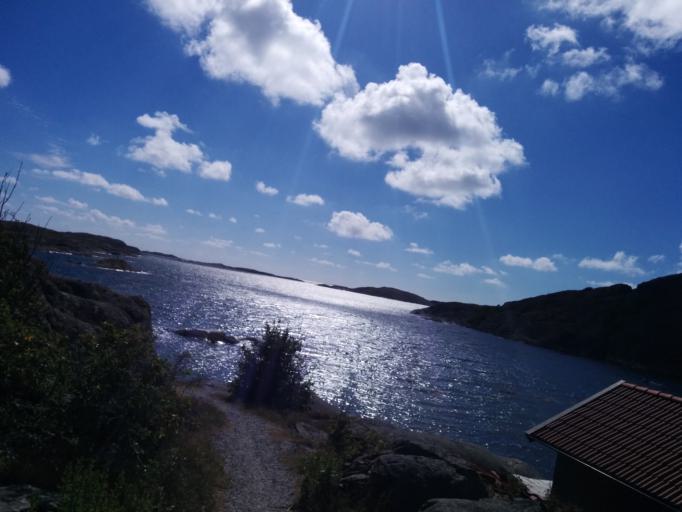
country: SE
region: Vaestra Goetaland
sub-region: Lysekils Kommun
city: Lysekil
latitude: 58.1230
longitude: 11.4387
